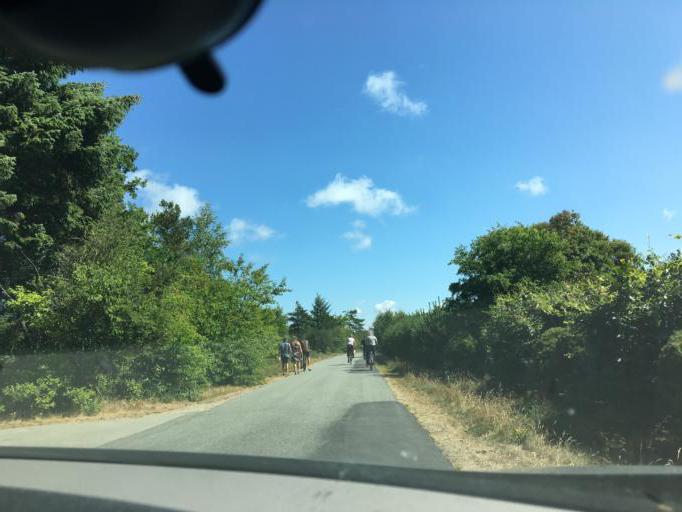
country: DK
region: South Denmark
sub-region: Varde Kommune
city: Oksbol
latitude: 55.7359
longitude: 8.2091
